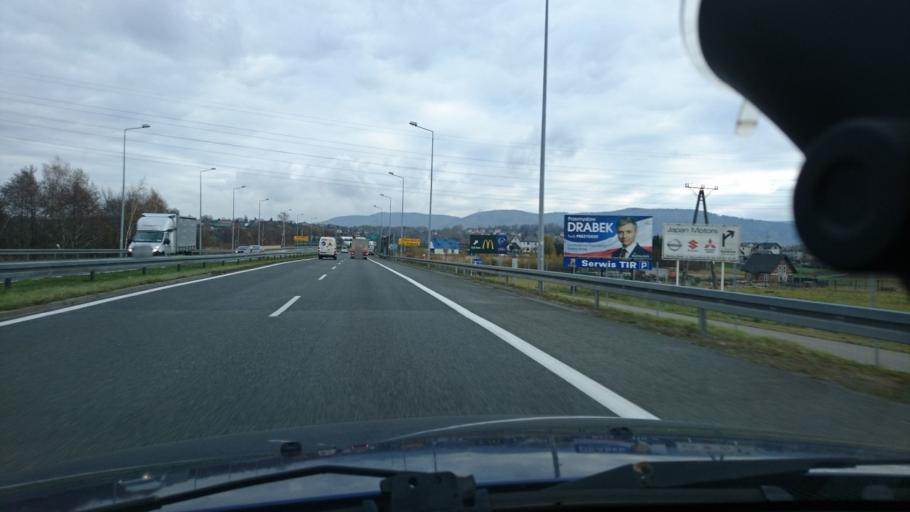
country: PL
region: Silesian Voivodeship
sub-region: Bielsko-Biala
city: Bielsko-Biala
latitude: 49.8474
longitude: 19.0598
